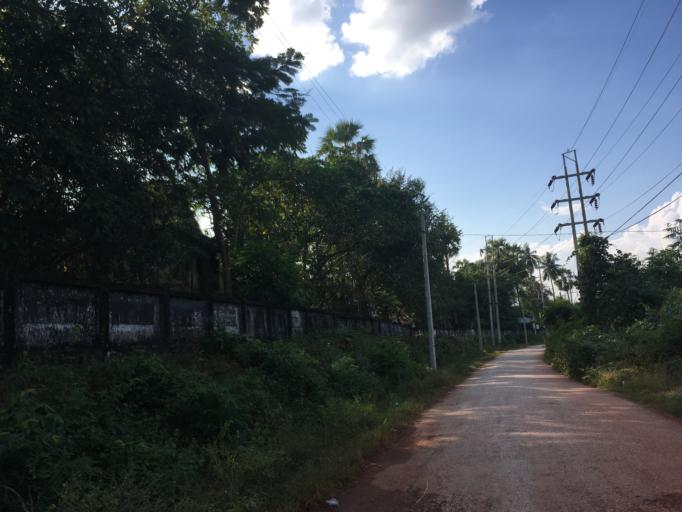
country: MM
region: Mon
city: Mawlamyine
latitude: 16.4284
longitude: 97.6243
